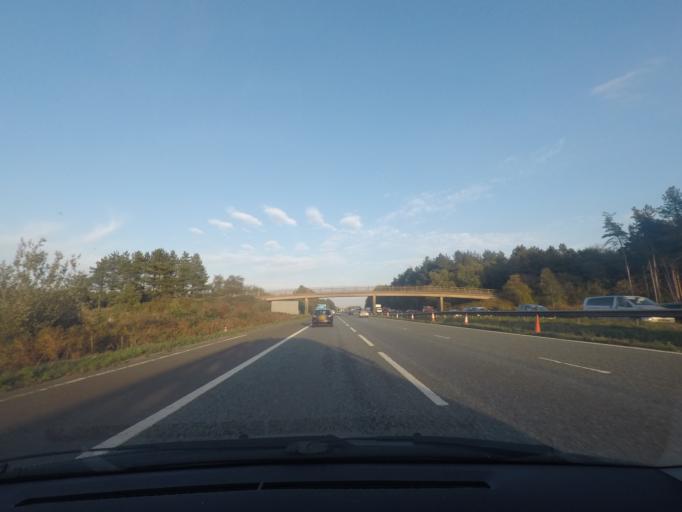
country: GB
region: England
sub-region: North Lincolnshire
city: Barnetby le Wold
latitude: 53.5818
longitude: -0.4374
